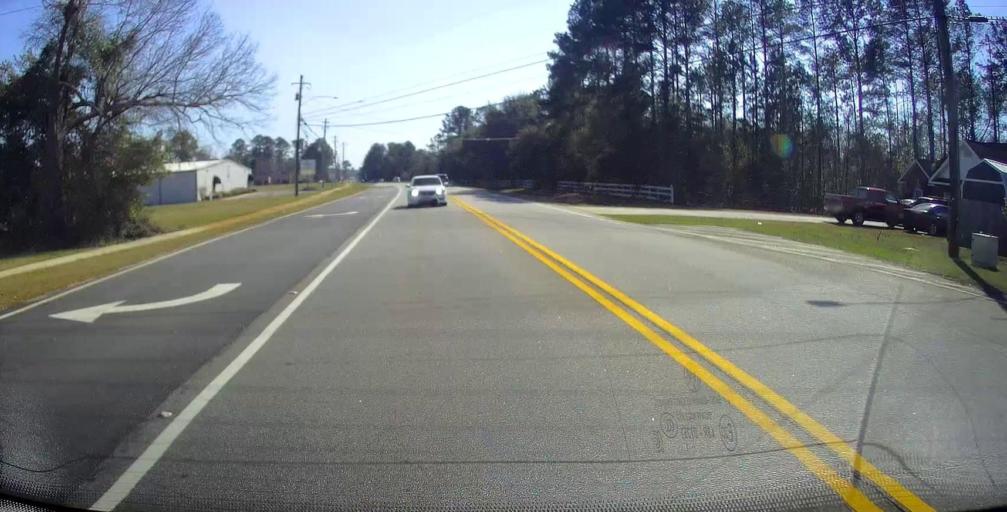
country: US
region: Georgia
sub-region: Houston County
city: Perry
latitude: 32.4780
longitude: -83.7300
